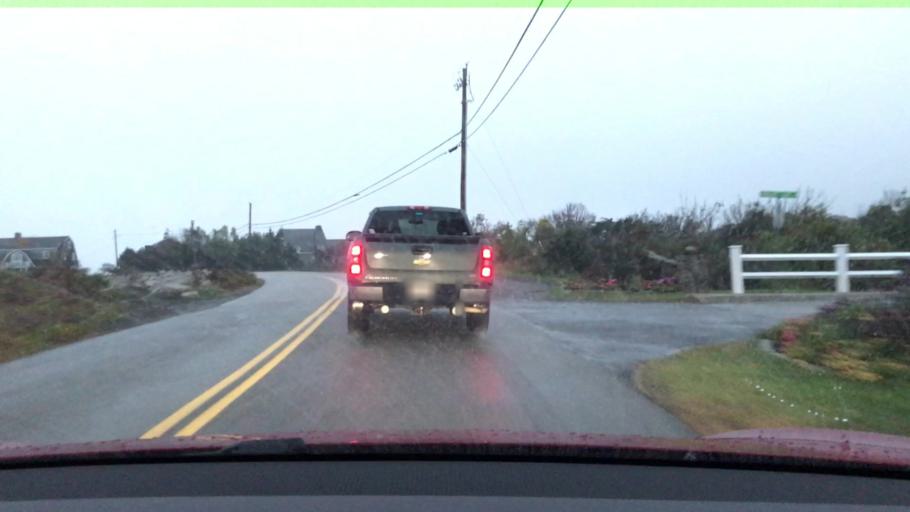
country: US
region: Maine
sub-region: York County
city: Cape Neddick
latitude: 43.2069
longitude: -70.5900
